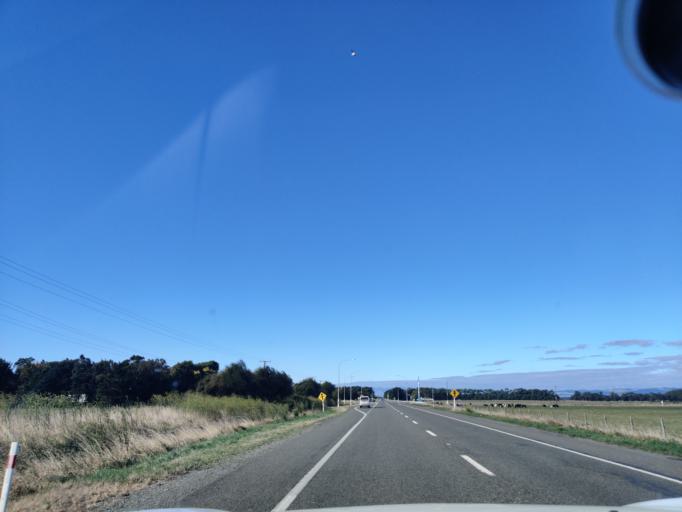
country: NZ
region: Manawatu-Wanganui
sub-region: Palmerston North City
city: Palmerston North
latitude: -40.4040
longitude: 175.4979
